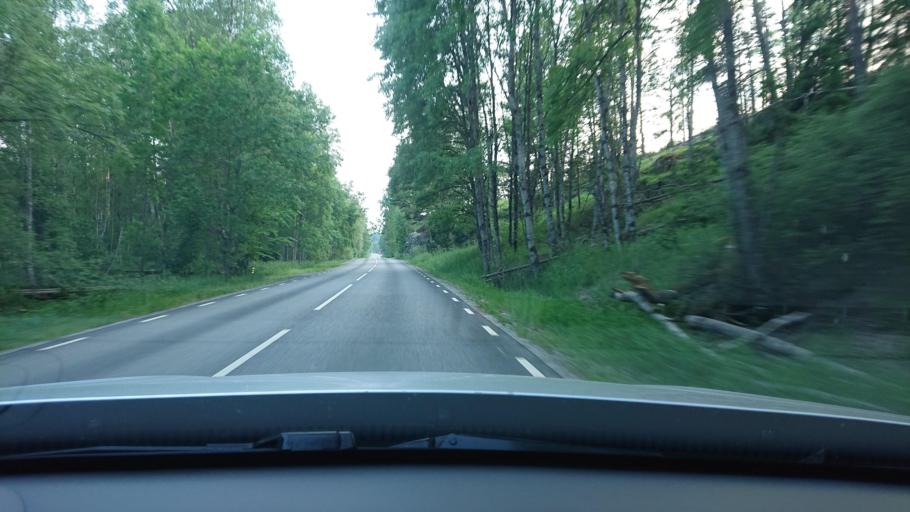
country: SE
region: Stockholm
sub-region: Vaxholms Kommun
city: Resaro
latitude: 59.4732
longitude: 18.3770
